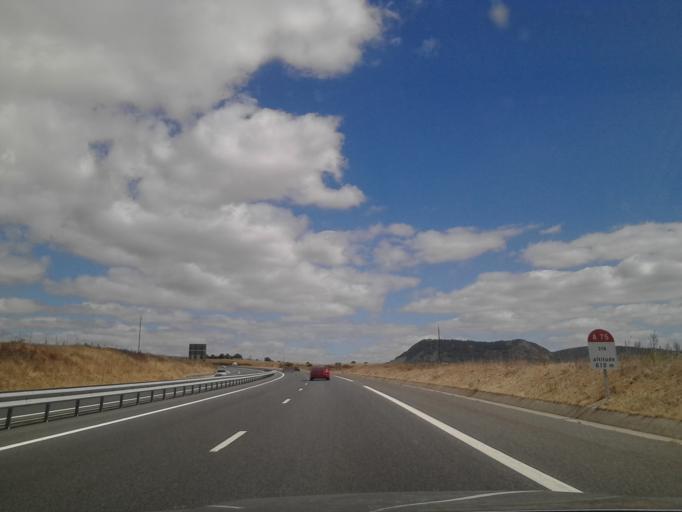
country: FR
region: Midi-Pyrenees
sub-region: Departement de l'Aveyron
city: Creissels
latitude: 44.1065
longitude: 3.0282
